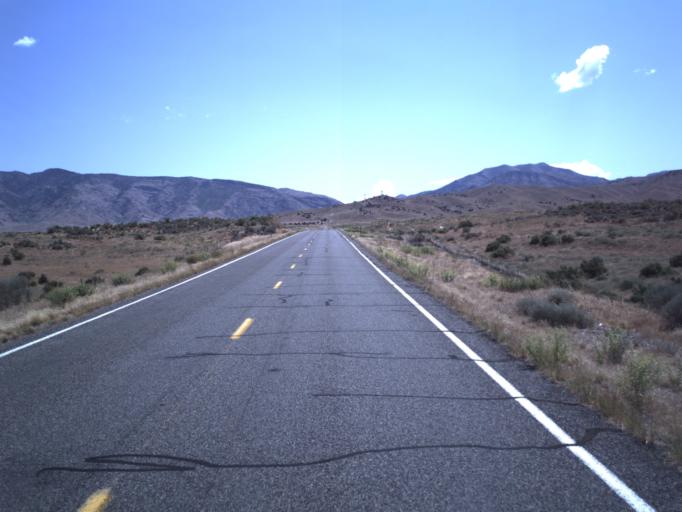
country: US
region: Utah
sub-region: Millard County
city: Delta
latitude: 39.3547
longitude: -112.3894
